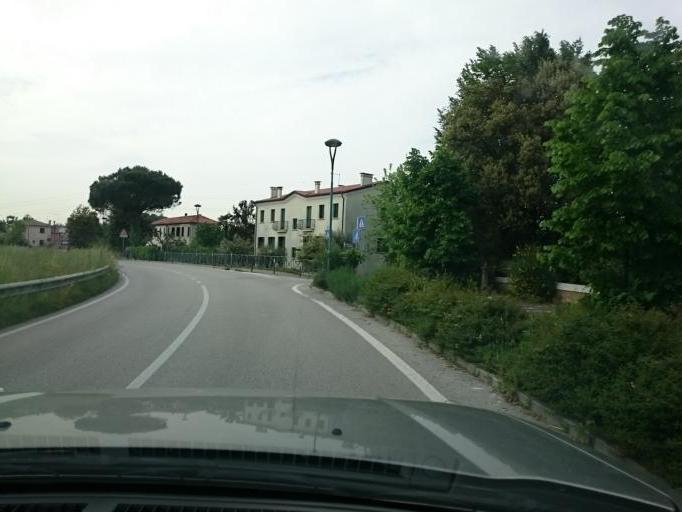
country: IT
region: Veneto
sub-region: Provincia di Venezia
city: Mestre
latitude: 45.4373
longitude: 12.2023
